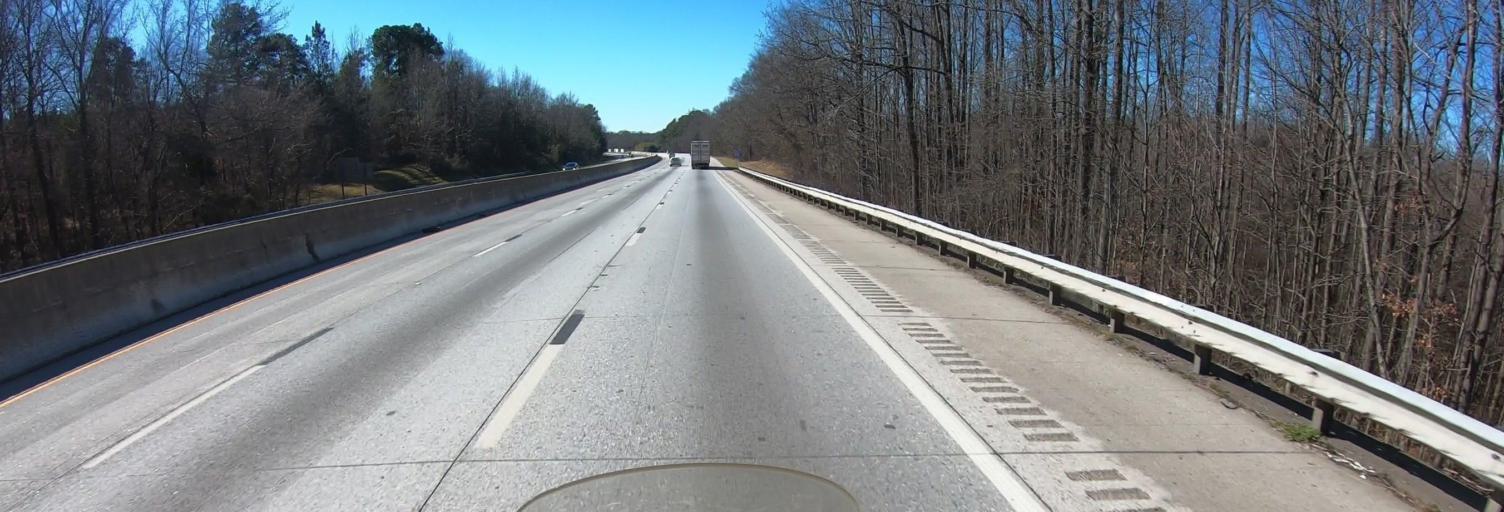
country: US
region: South Carolina
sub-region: Anderson County
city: Piedmont
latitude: 34.6739
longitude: -82.5453
